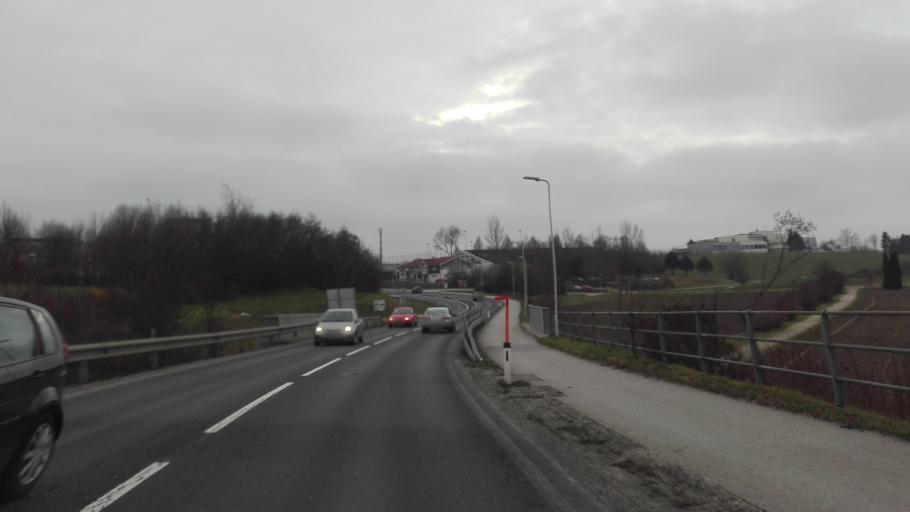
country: AT
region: Upper Austria
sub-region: Politischer Bezirk Linz-Land
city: Leonding
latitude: 48.2719
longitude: 14.2574
